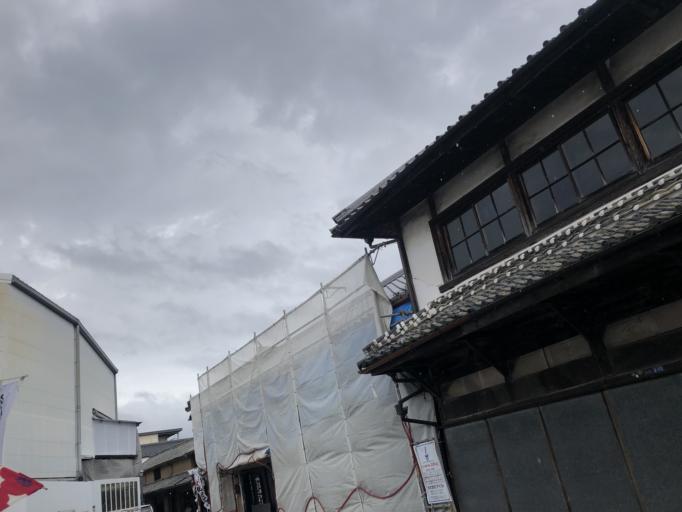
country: JP
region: Oita
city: Hita
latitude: 33.3260
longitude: 130.9357
